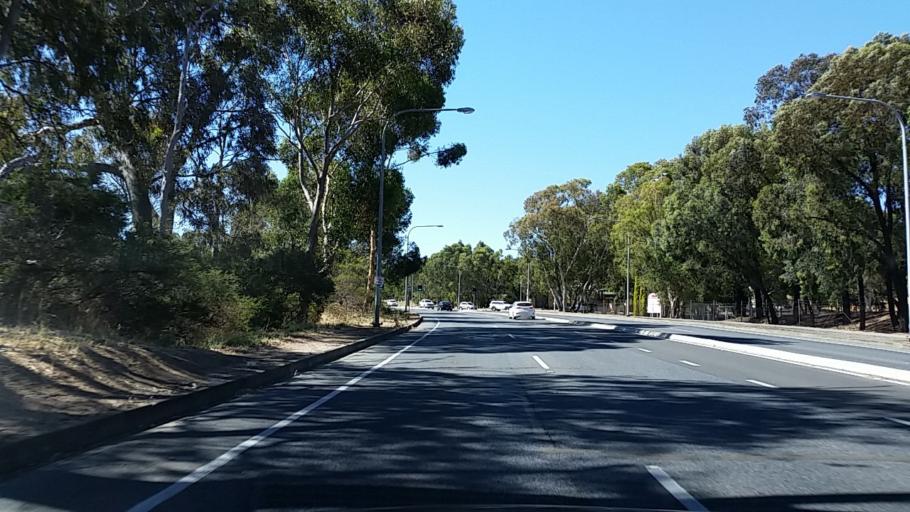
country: AU
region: South Australia
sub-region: Tea Tree Gully
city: Hope Valley
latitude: -34.8186
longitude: 138.6951
